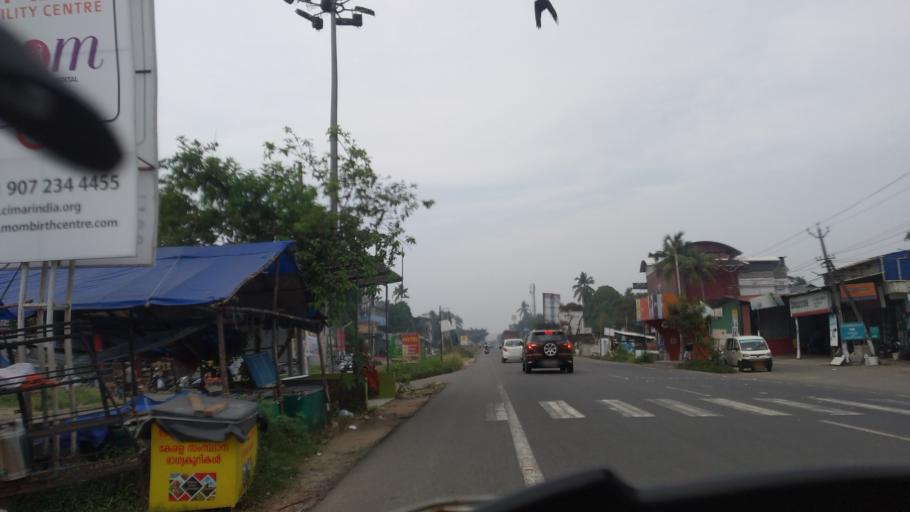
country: IN
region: Kerala
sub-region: Ernakulam
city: Elur
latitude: 10.0508
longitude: 76.2939
